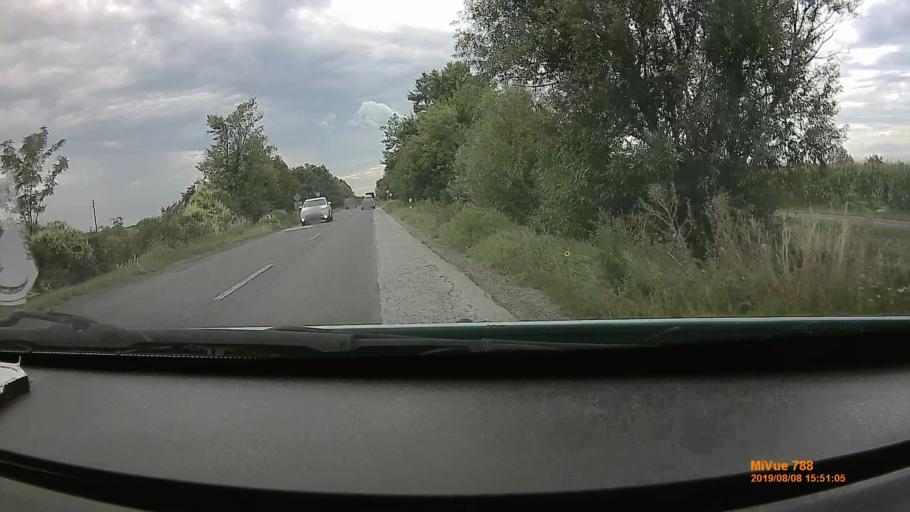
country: HU
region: Szabolcs-Szatmar-Bereg
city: Mateszalka
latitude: 47.9411
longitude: 22.3508
